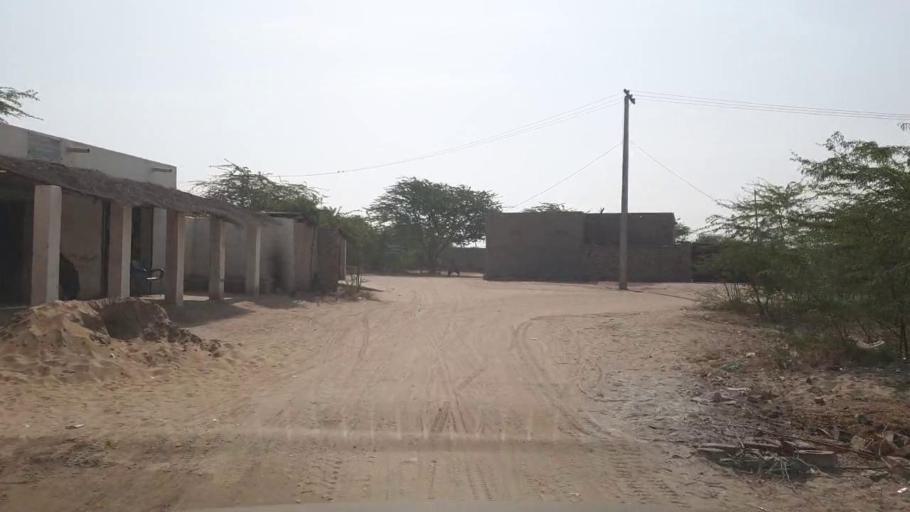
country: PK
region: Sindh
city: Umarkot
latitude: 25.3344
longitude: 69.7348
